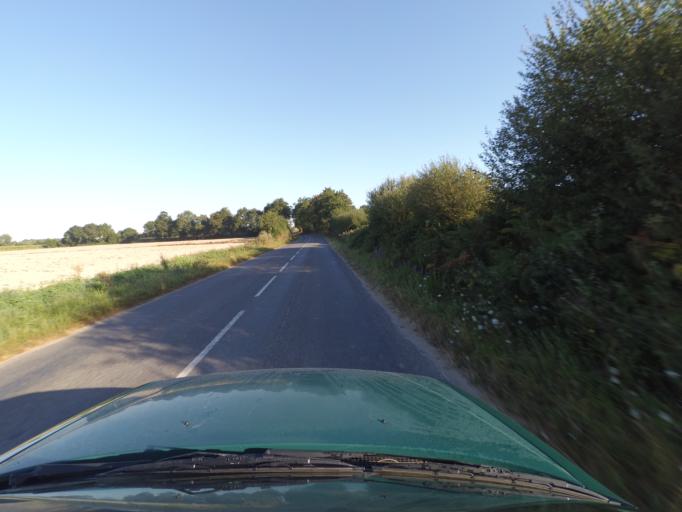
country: FR
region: Pays de la Loire
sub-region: Departement de la Loire-Atlantique
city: La Planche
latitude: 47.0233
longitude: -1.4617
